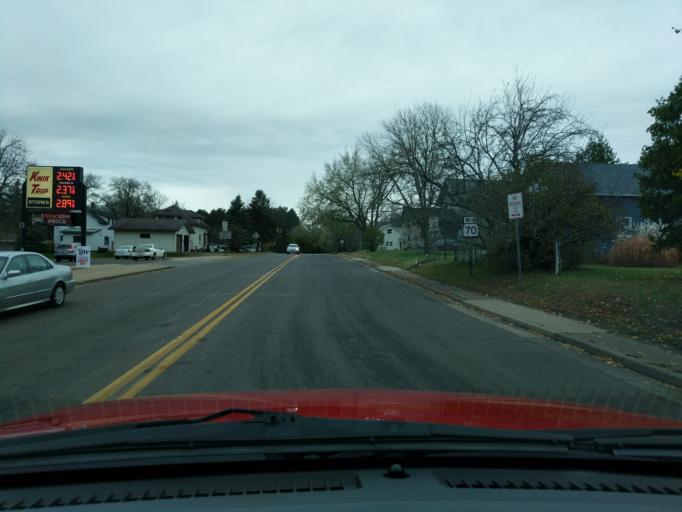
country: US
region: Wisconsin
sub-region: Washburn County
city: Spooner
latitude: 45.8230
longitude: -91.8910
